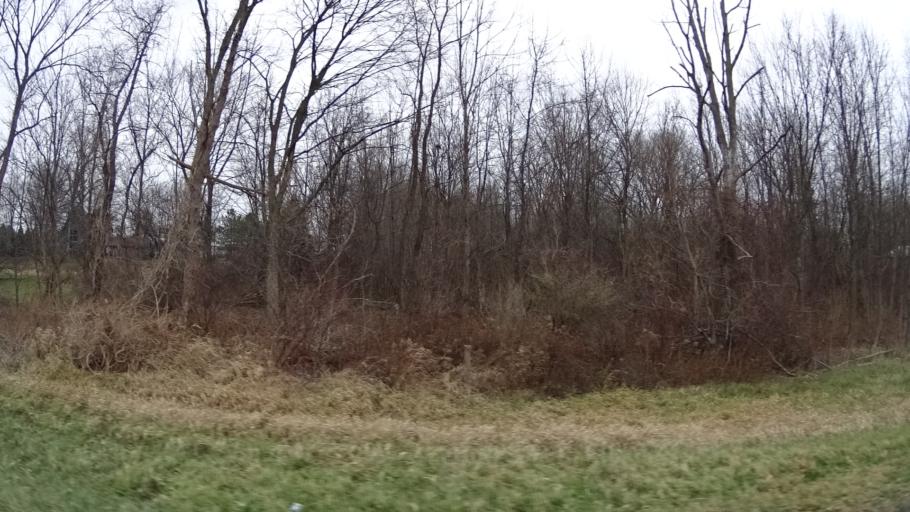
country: US
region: Ohio
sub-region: Lorain County
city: Camden
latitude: 41.1713
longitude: -82.3121
